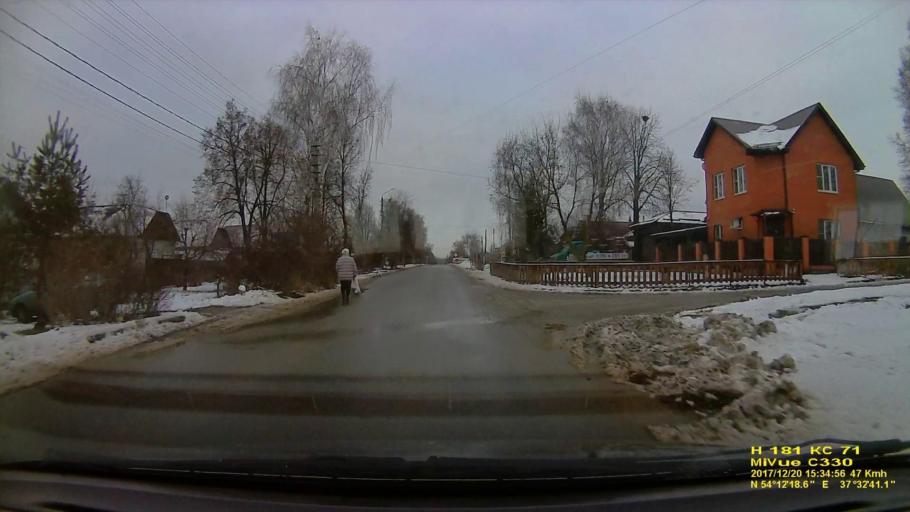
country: RU
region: Tula
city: Tula
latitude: 54.2051
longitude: 37.5448
